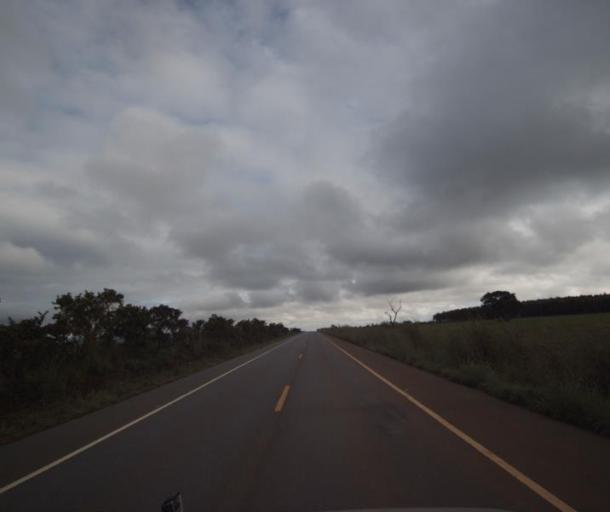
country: BR
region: Goias
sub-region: Padre Bernardo
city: Padre Bernardo
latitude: -15.3312
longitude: -48.6506
